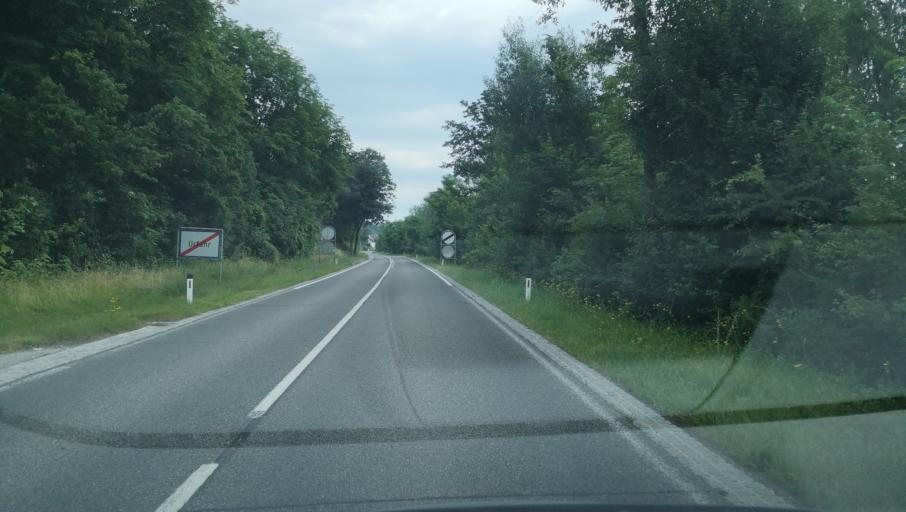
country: AT
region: Lower Austria
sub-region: Politischer Bezirk Melk
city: Leiben
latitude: 48.2283
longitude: 15.2856
